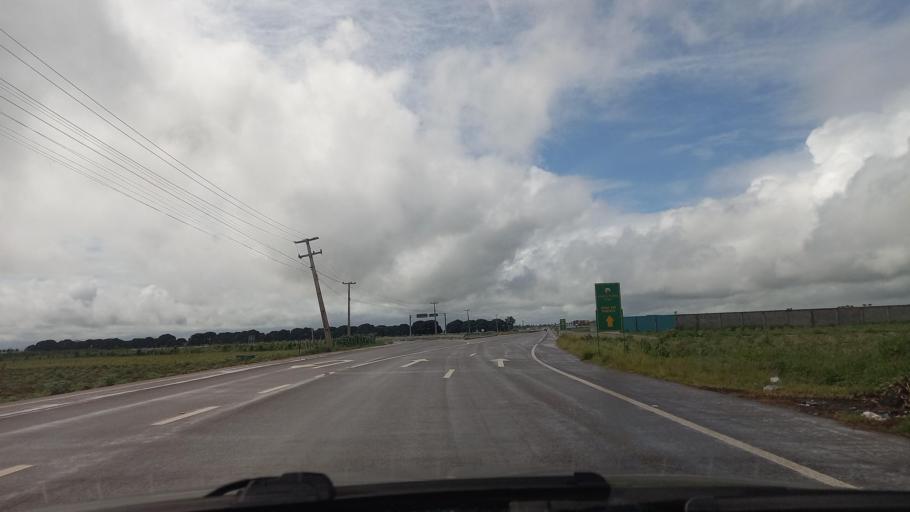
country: BR
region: Alagoas
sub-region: Limoeiro De Anadia
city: Limoeiro de Anadia
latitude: -9.7580
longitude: -36.5531
